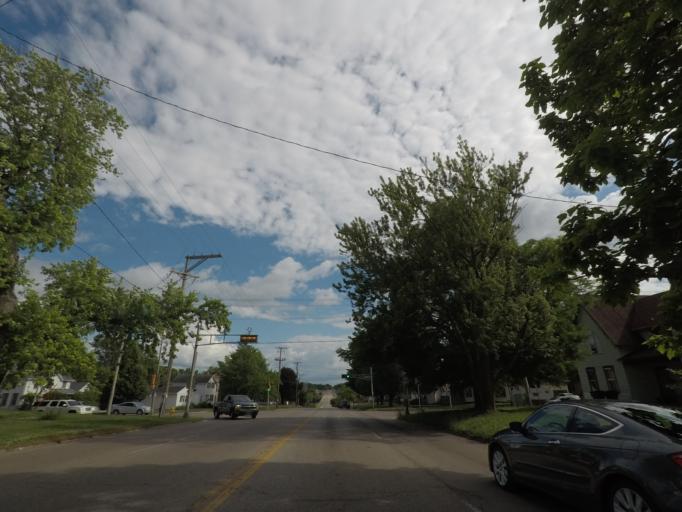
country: US
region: Wisconsin
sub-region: Rock County
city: Janesville
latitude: 42.6746
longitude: -89.0318
